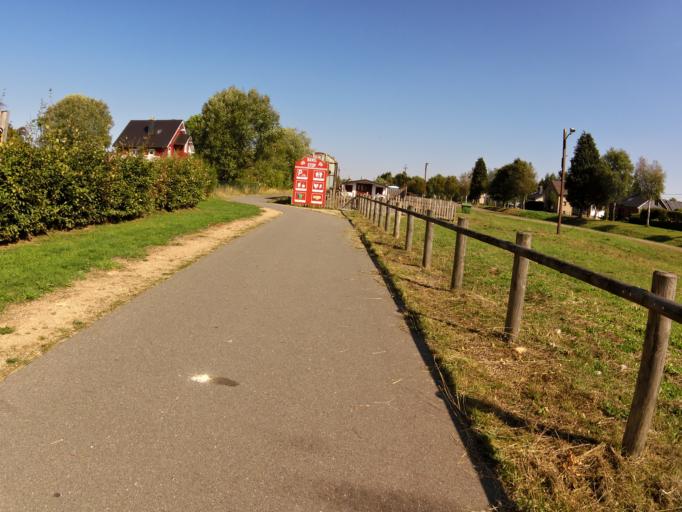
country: BE
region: Wallonia
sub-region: Province de Liege
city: Waimes
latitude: 50.4741
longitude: 6.1444
